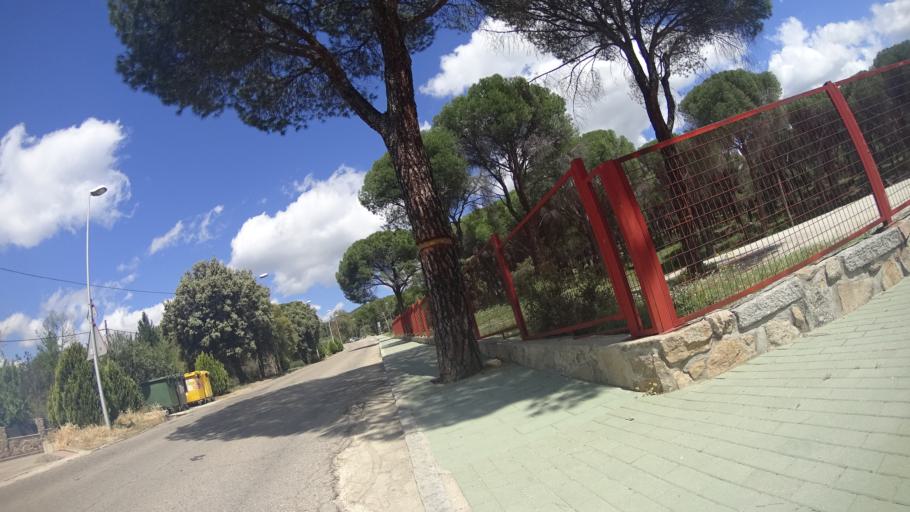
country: ES
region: Madrid
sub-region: Provincia de Madrid
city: Pelayos de la Presa
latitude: 40.3631
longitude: -4.3303
